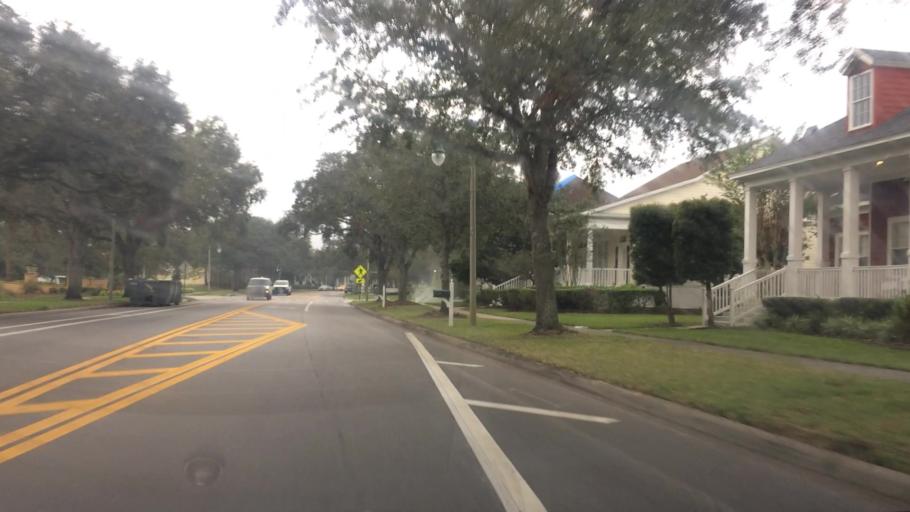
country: US
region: Florida
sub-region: Osceola County
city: Celebration
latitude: 28.3219
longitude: -81.5353
